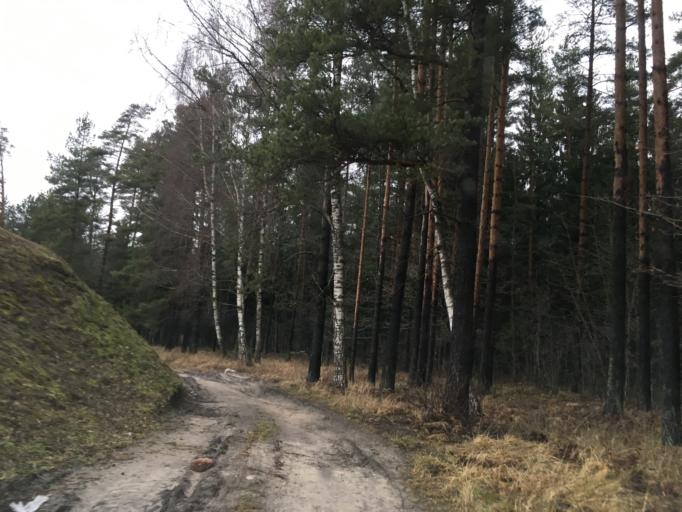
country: LV
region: Ozolnieku
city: Ozolnieki
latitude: 56.6932
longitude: 23.7841
